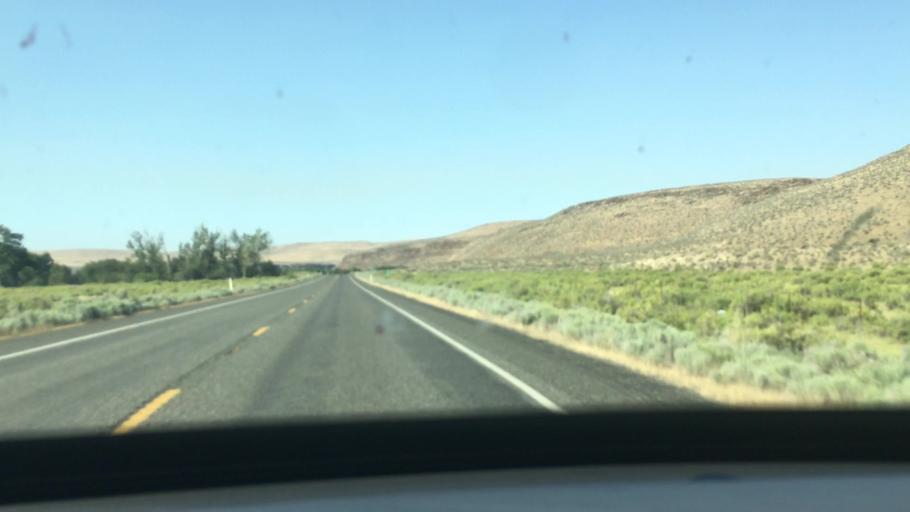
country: US
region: Washington
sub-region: Yakima County
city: Toppenish
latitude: 46.2274
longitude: -120.4255
